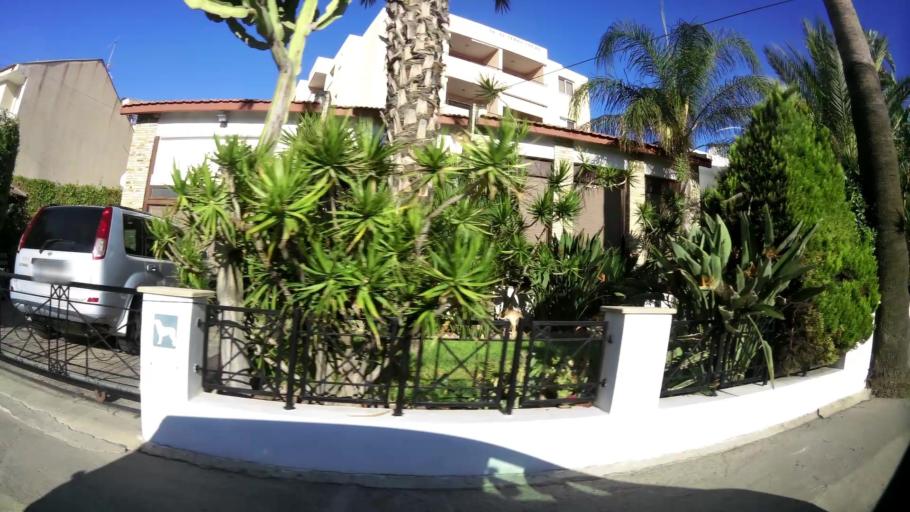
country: CY
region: Larnaka
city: Larnaca
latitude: 34.9239
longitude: 33.6258
